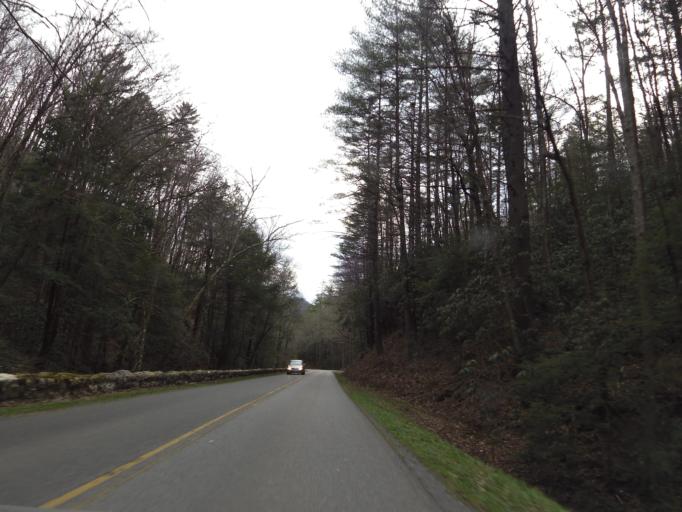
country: US
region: Tennessee
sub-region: Blount County
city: Wildwood
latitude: 35.6162
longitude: -83.7412
